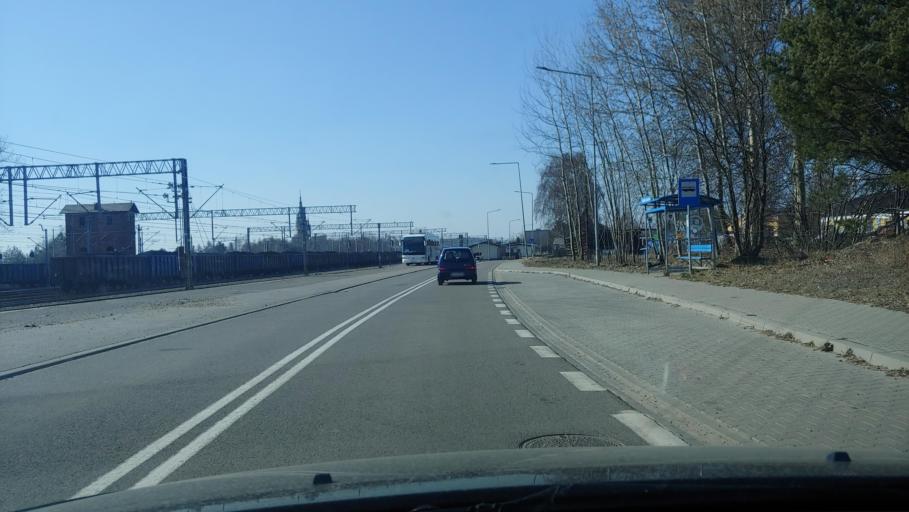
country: PL
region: Lesser Poland Voivodeship
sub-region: Powiat chrzanowski
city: Trzebinia
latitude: 50.1528
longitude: 19.4591
